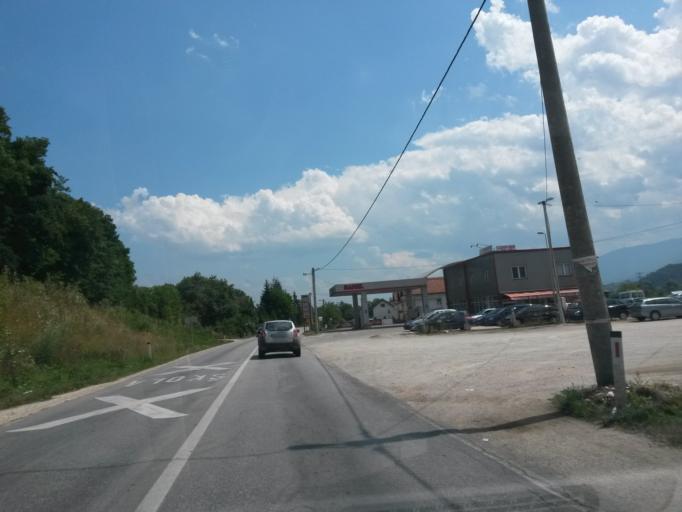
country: BA
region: Federation of Bosnia and Herzegovina
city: Vitez
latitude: 44.1892
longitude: 17.7393
